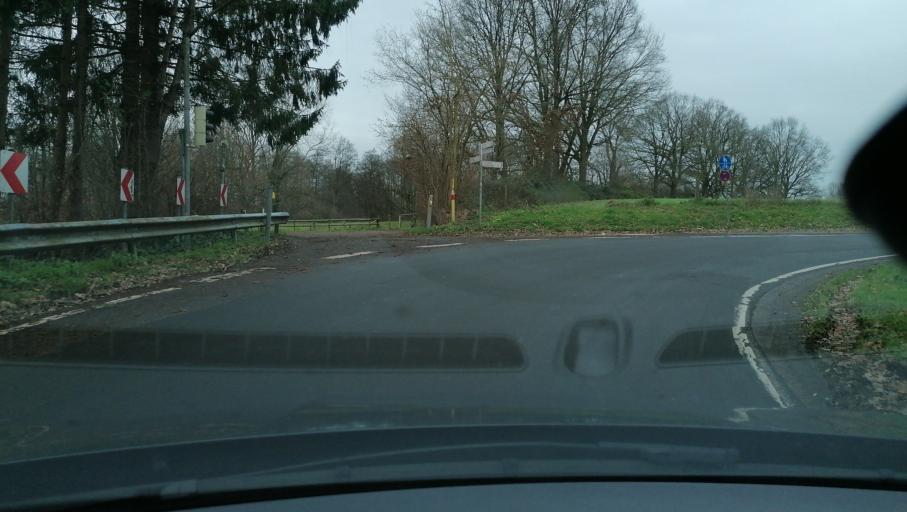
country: DE
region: North Rhine-Westphalia
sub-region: Regierungsbezirk Munster
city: Klein Reken
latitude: 51.7923
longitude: 7.0399
